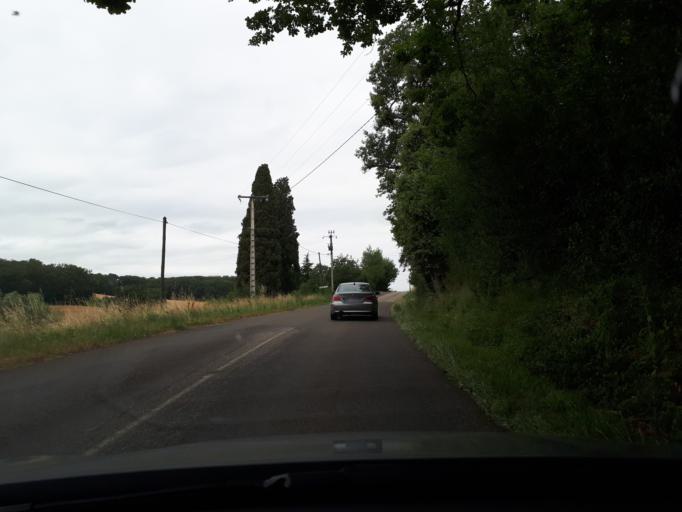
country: FR
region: Midi-Pyrenees
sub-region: Departement du Gers
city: Lectoure
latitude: 43.9297
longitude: 0.5793
